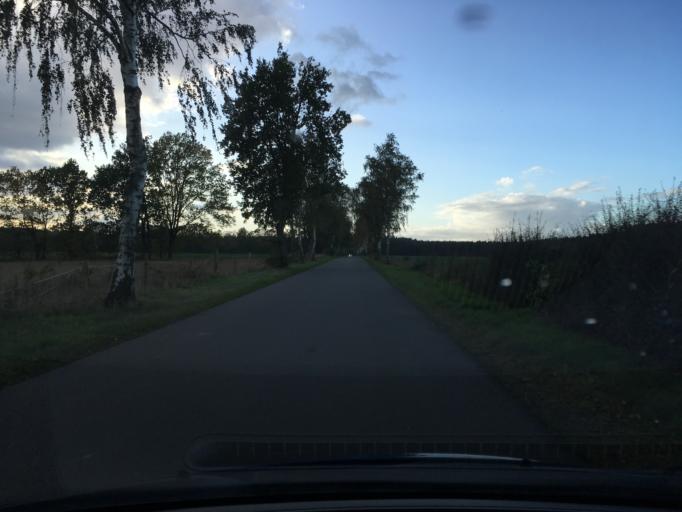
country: DE
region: Lower Saxony
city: Reinstorf
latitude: 53.2504
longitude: 10.5472
